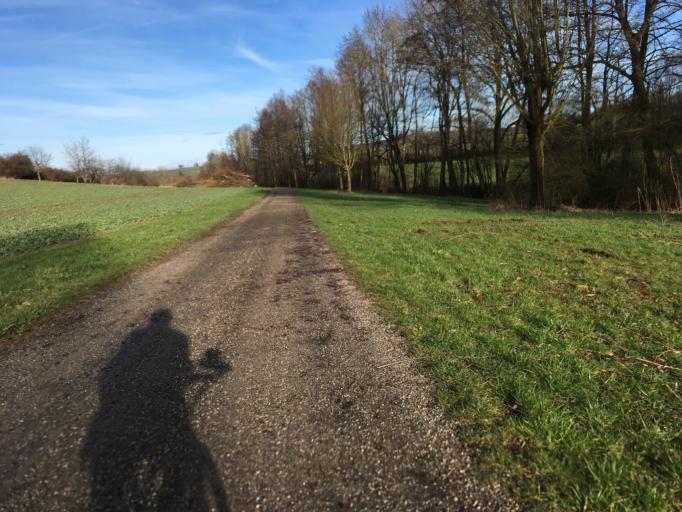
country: DE
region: Baden-Wuerttemberg
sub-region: Regierungsbezirk Stuttgart
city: Lehrensteinsfeld
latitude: 49.1233
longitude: 9.3573
